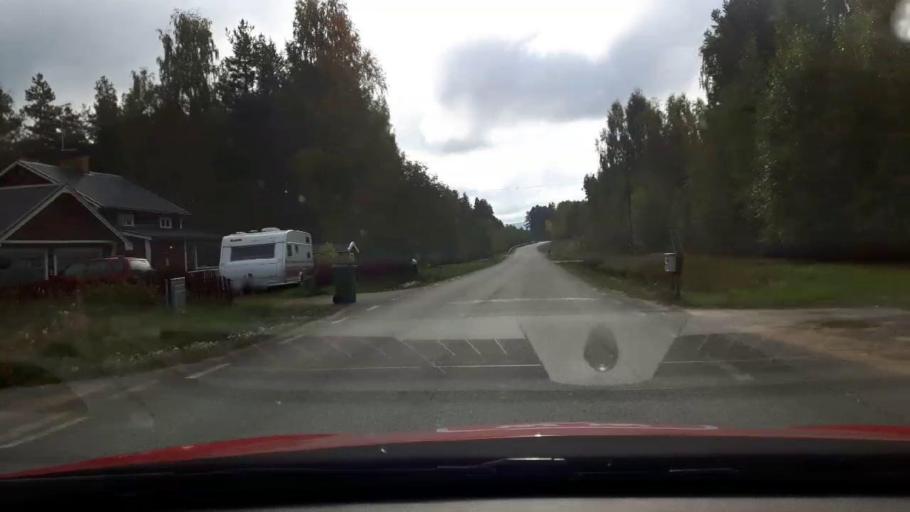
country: SE
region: Gaevleborg
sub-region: Ljusdals Kommun
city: Farila
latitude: 61.7968
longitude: 15.9115
